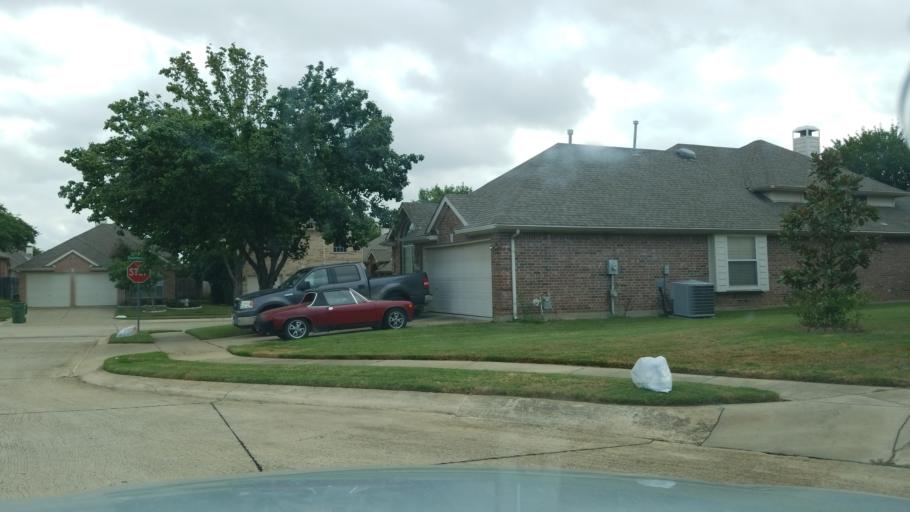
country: US
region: Texas
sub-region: Tarrant County
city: Euless
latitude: 32.8405
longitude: -97.1054
